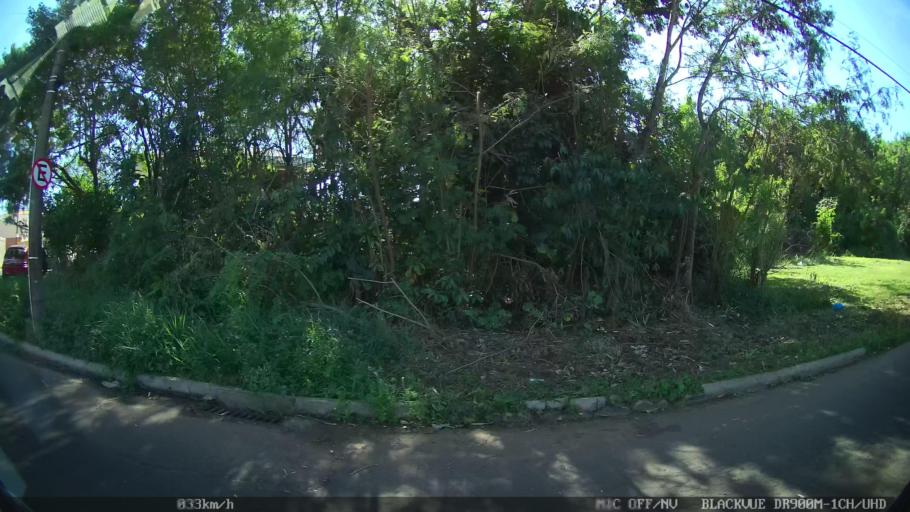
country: BR
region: Sao Paulo
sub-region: Batatais
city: Batatais
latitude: -20.8847
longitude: -47.5843
